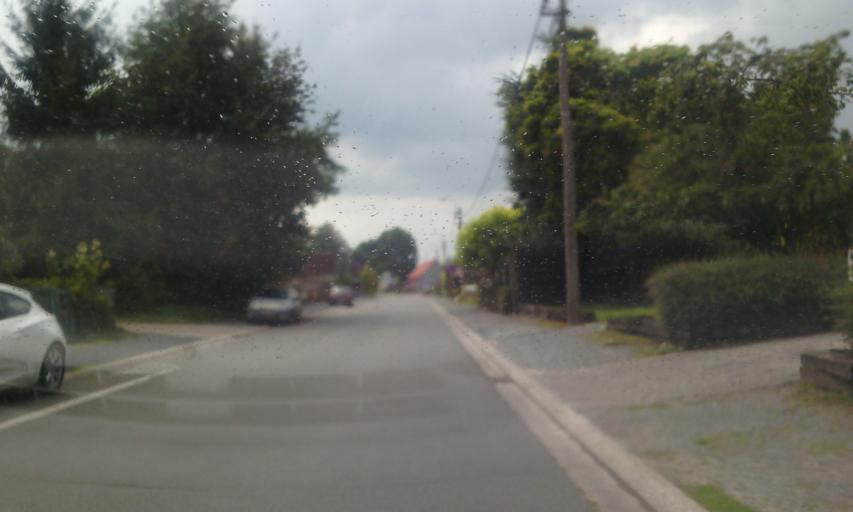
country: BE
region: Flanders
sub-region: Provincie Oost-Vlaanderen
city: Lokeren
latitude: 51.1053
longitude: 3.9587
